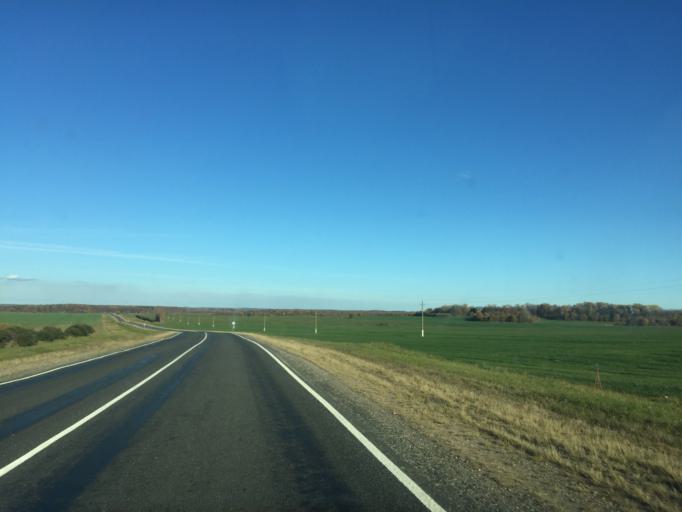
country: BY
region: Vitebsk
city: Dzisna
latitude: 55.3051
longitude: 28.2536
